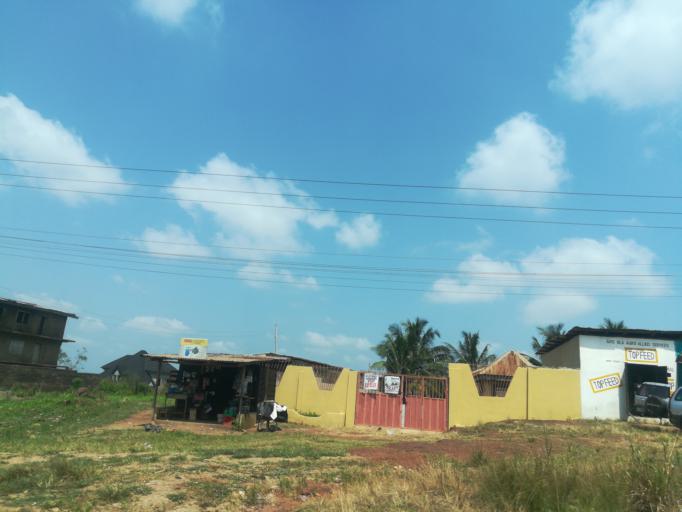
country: NG
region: Ogun
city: Abeokuta
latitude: 7.1398
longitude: 3.4038
